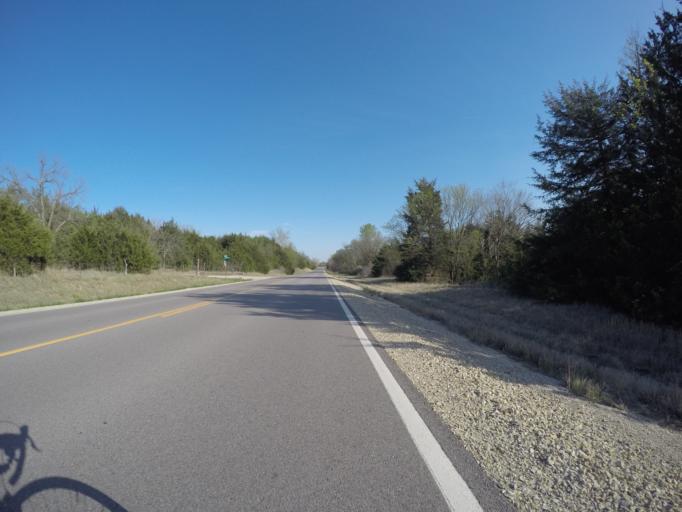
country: US
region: Kansas
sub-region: Riley County
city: Fort Riley North
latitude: 39.2444
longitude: -96.7663
